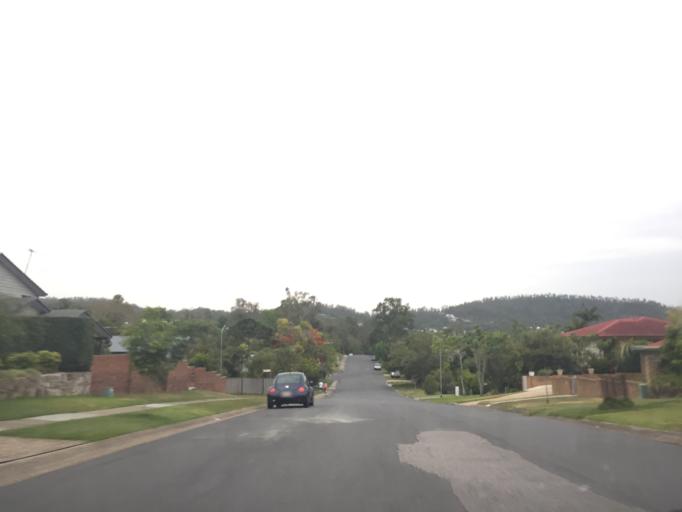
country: AU
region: Queensland
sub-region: Moreton Bay
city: Ferny Hills
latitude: -27.4422
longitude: 152.9347
